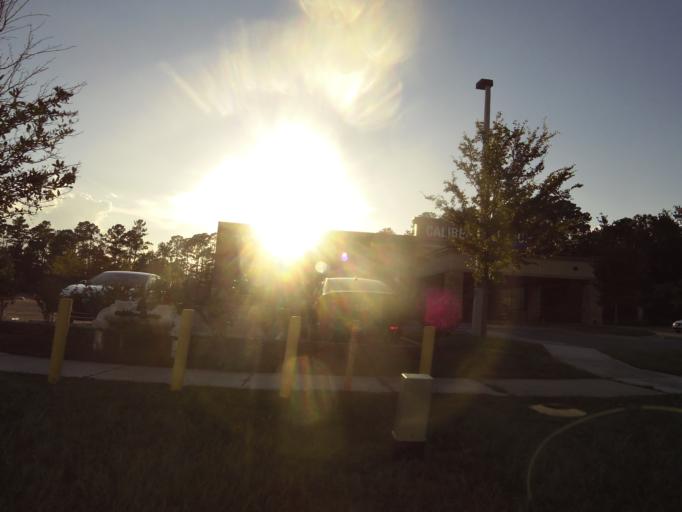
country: US
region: Florida
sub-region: Clay County
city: Orange Park
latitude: 30.2257
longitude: -81.7026
